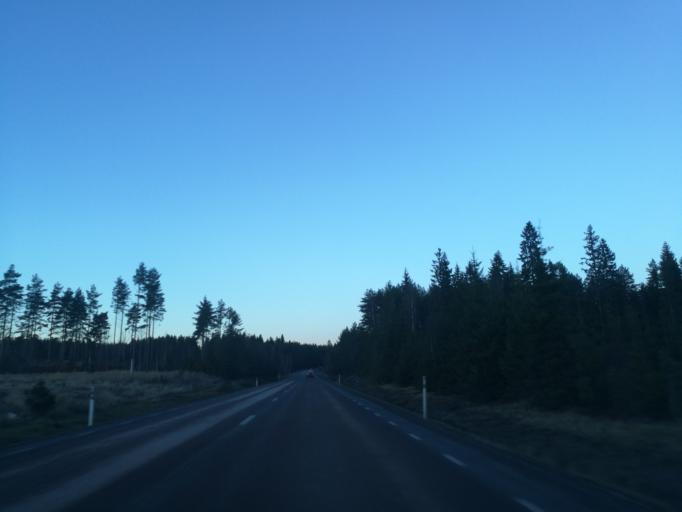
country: SE
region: Vaermland
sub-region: Eda Kommun
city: Charlottenberg
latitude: 59.8935
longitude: 12.2797
